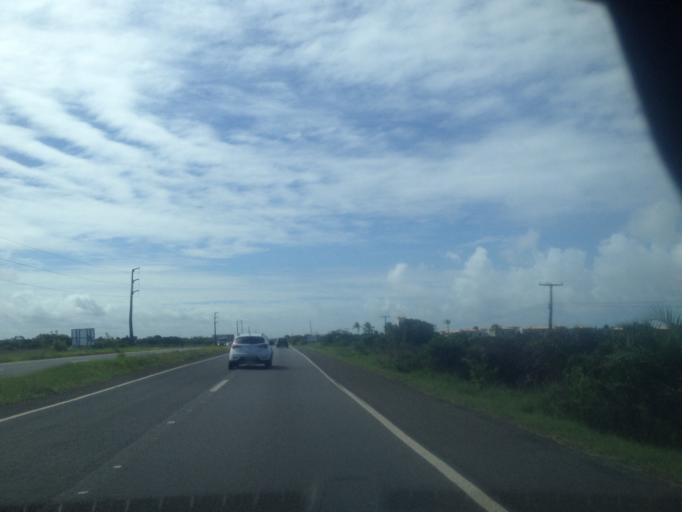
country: BR
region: Bahia
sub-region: Camacari
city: Camacari
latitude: -12.6667
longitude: -38.0951
